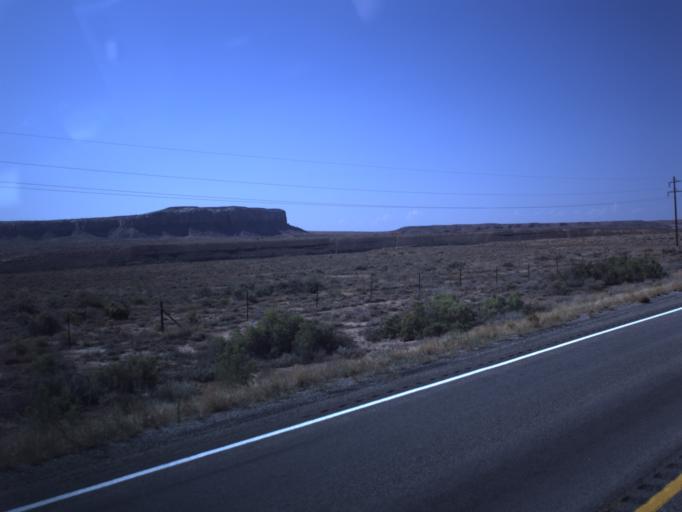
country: US
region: Utah
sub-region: San Juan County
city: Blanding
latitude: 37.2710
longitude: -109.5968
